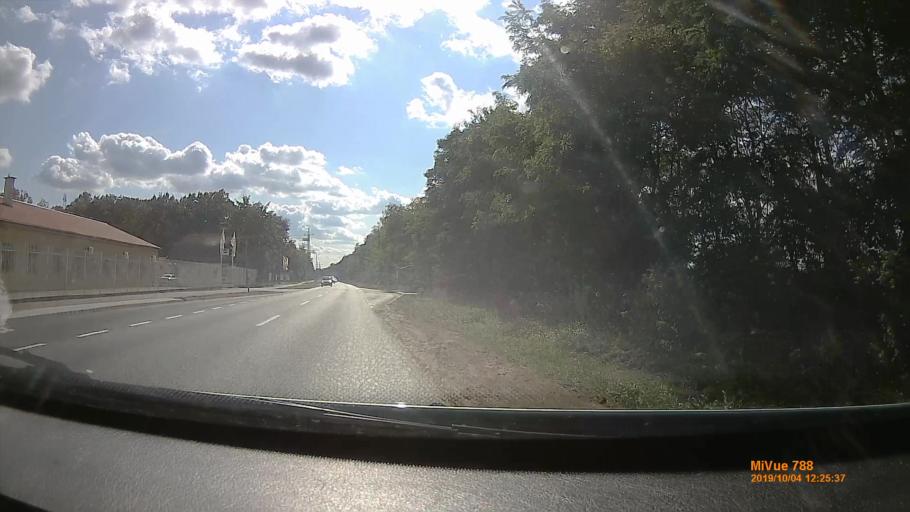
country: HU
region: Szabolcs-Szatmar-Bereg
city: Nyiregyhaza
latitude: 47.9843
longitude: 21.7044
